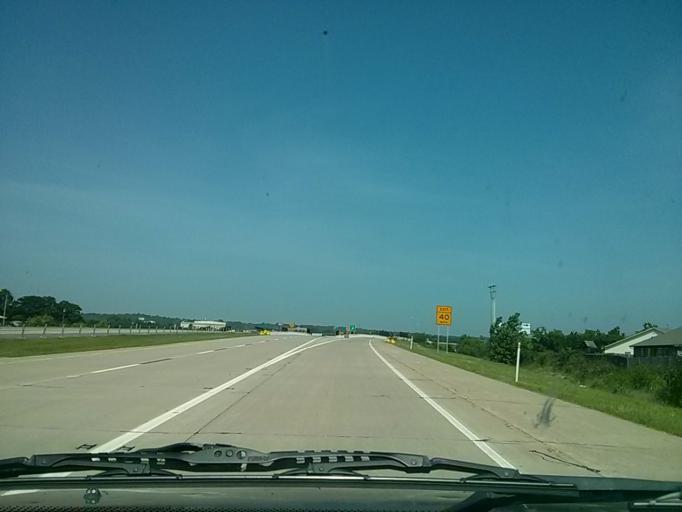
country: US
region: Oklahoma
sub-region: Creek County
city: Sapulpa
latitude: 36.0285
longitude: -96.0818
